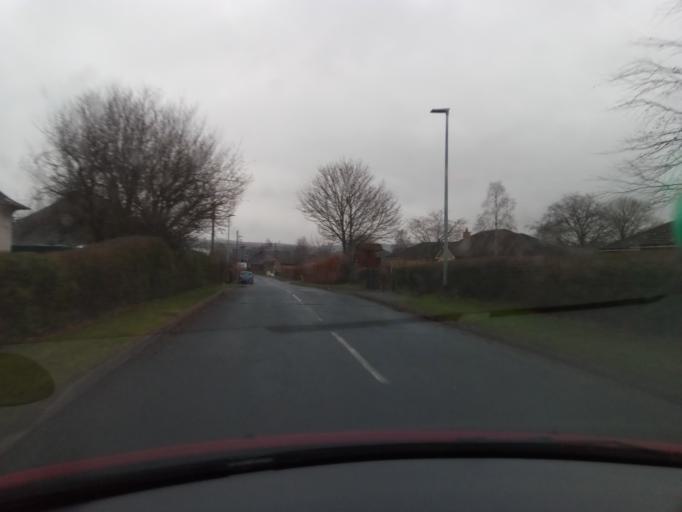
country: GB
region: Scotland
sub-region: The Scottish Borders
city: Kelso
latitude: 55.5272
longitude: -2.4632
